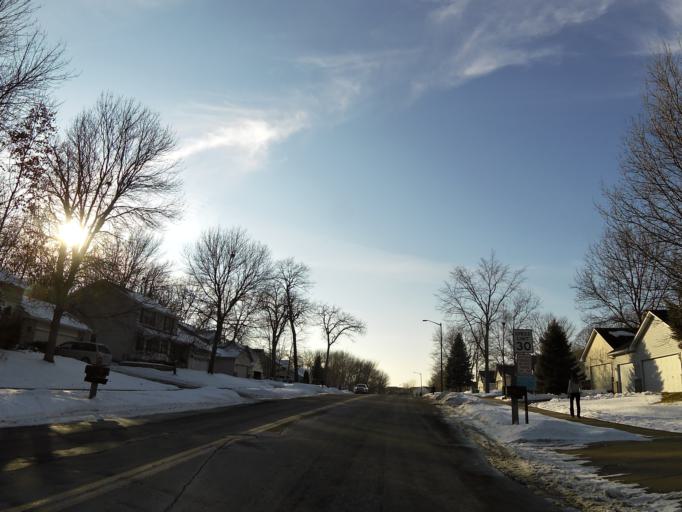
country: US
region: Minnesota
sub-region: Scott County
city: Savage
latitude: 44.7354
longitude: -93.3515
